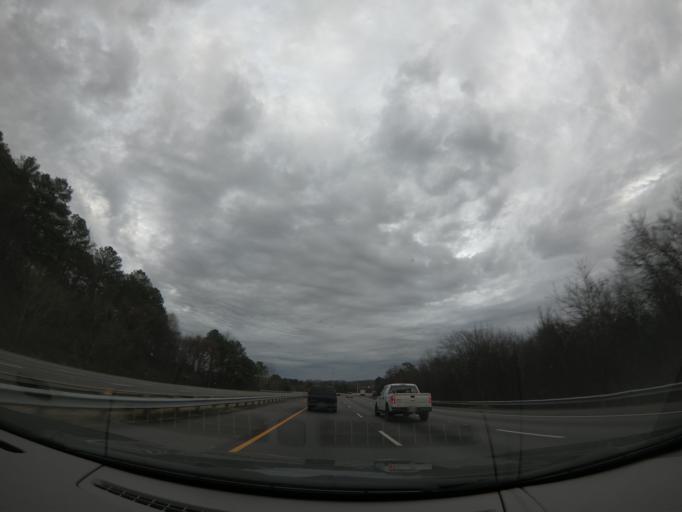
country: US
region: Georgia
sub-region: Whitfield County
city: Dalton
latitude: 34.7994
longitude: -85.0059
